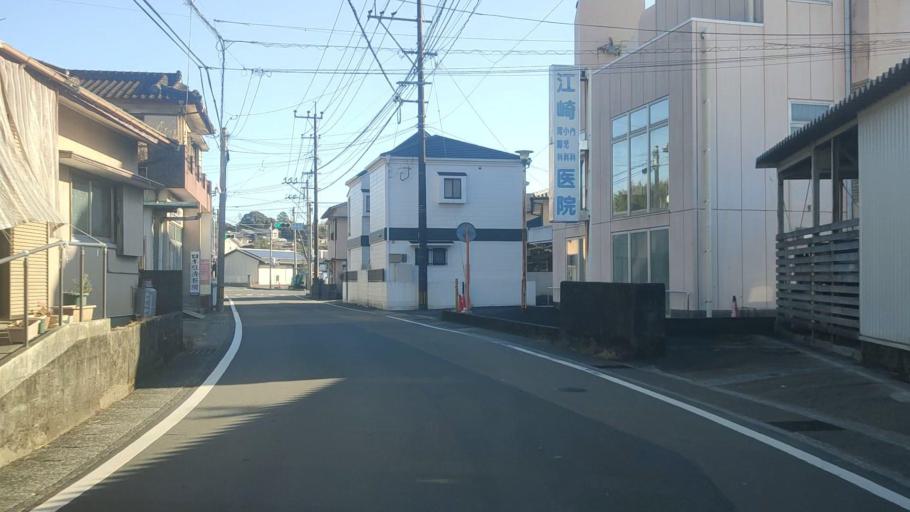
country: JP
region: Miyazaki
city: Nobeoka
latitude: 32.6093
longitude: 131.6873
